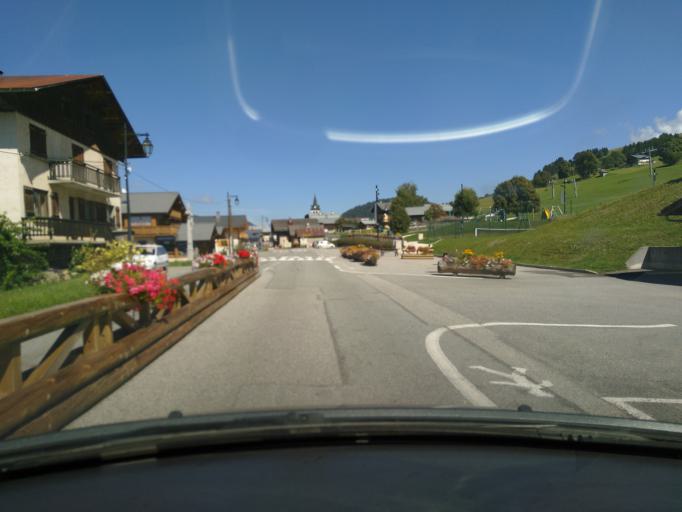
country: FR
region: Rhone-Alpes
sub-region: Departement de la Haute-Savoie
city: Praz-sur-Arly
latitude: 45.7930
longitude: 6.5025
